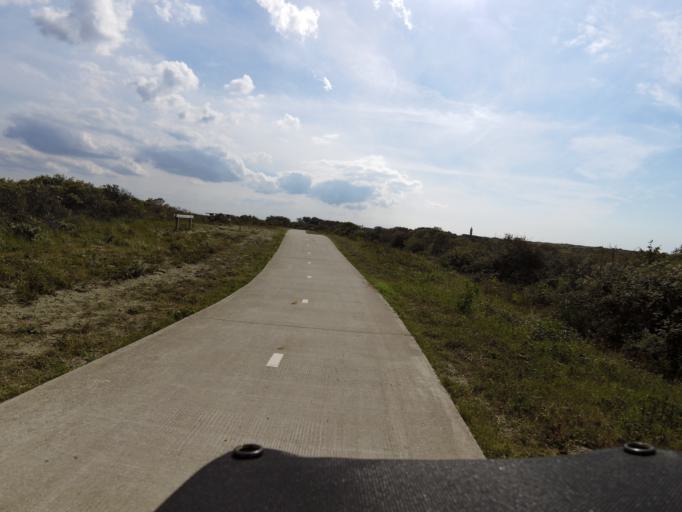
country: NL
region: South Holland
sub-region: Gemeente Goeree-Overflakkee
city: Ouddorp
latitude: 51.8207
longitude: 3.8857
